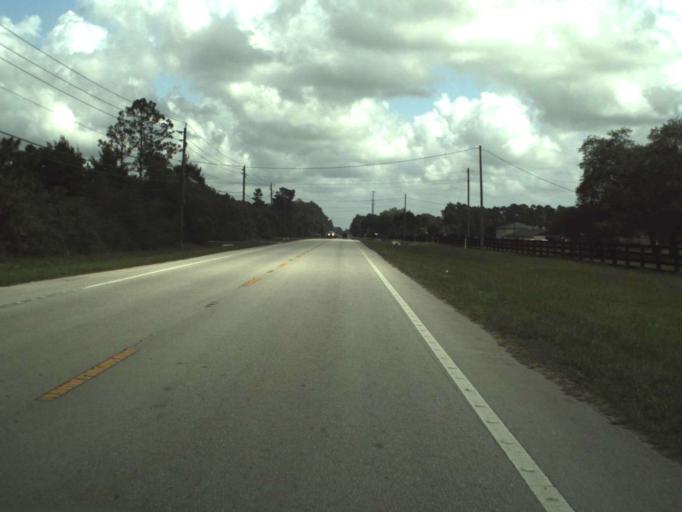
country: US
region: Florida
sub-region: Volusia County
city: Samsula-Spruce Creek
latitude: 28.9947
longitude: -81.0714
